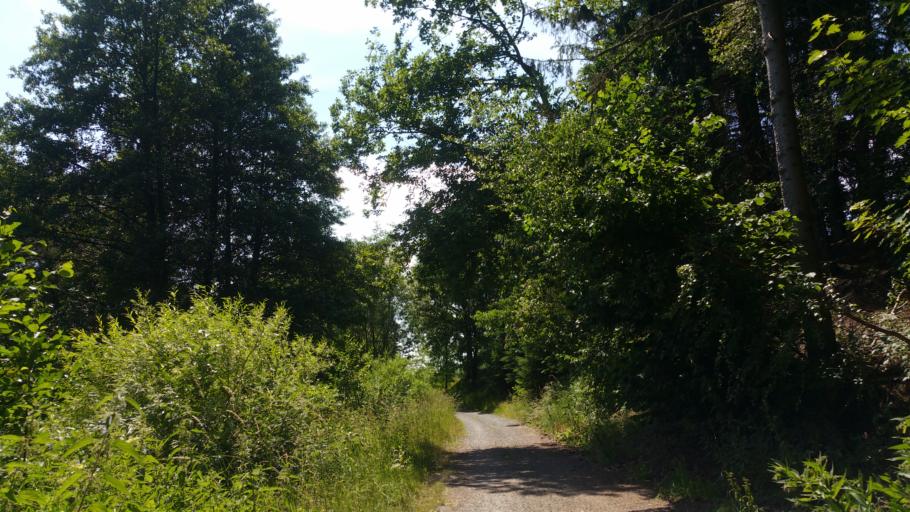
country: DE
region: Bavaria
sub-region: Upper Franconia
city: Schwarzenbach an der Saale
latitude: 50.2149
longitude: 11.9217
